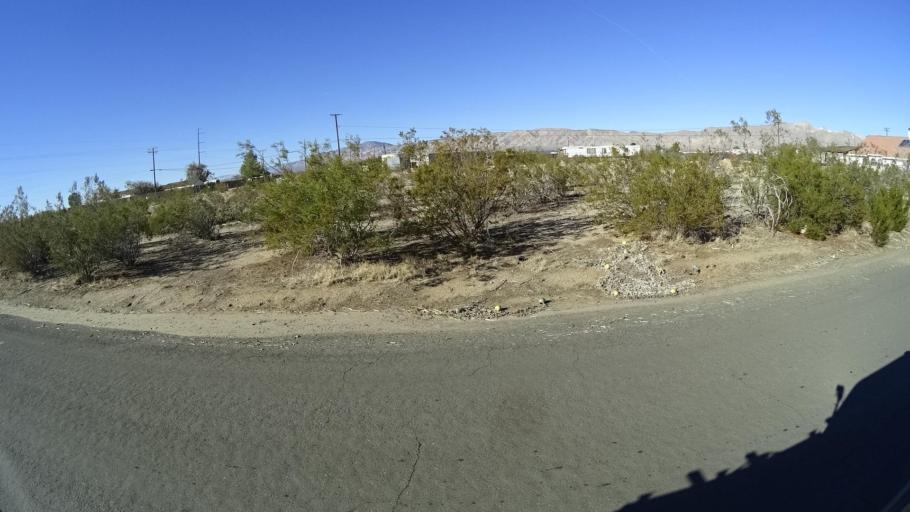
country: US
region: California
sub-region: Kern County
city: California City
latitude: 35.1998
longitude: -118.0125
